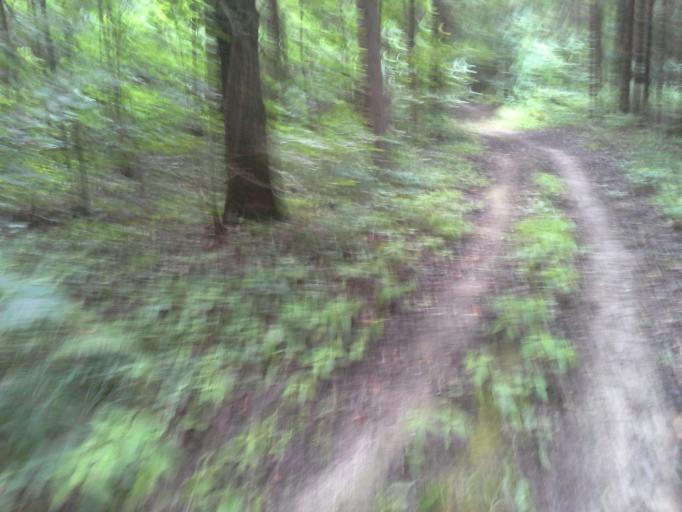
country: RU
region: Moskovskaya
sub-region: Leninskiy Rayon
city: Vnukovo
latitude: 55.6437
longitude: 37.2966
